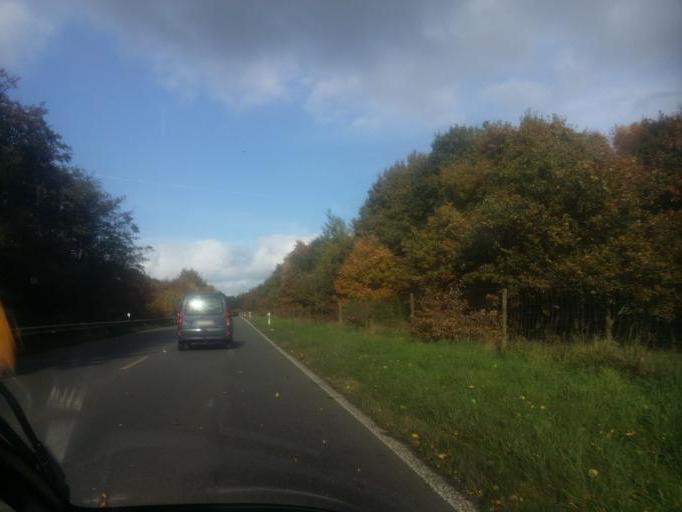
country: DE
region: Schleswig-Holstein
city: Pinneberg
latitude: 53.6331
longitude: 9.7759
